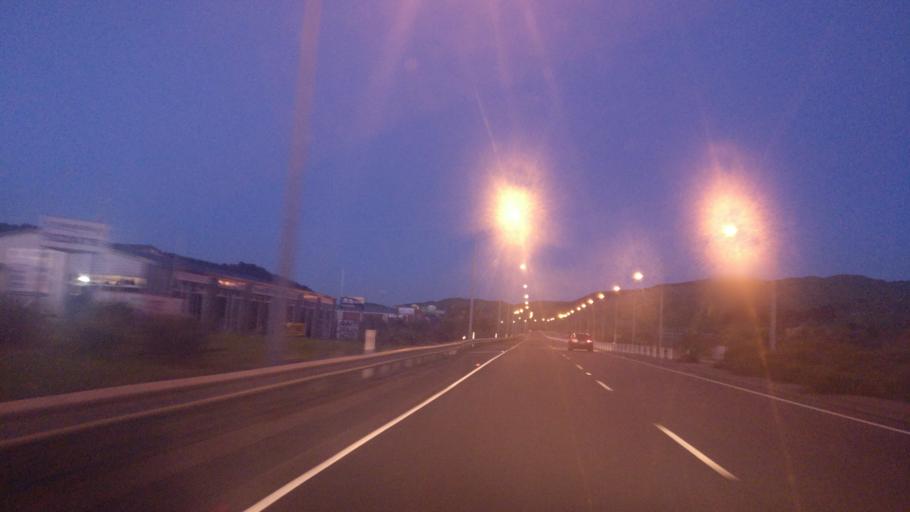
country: NZ
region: Wellington
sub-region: Porirua City
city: Porirua
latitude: -41.0817
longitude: 174.8700
